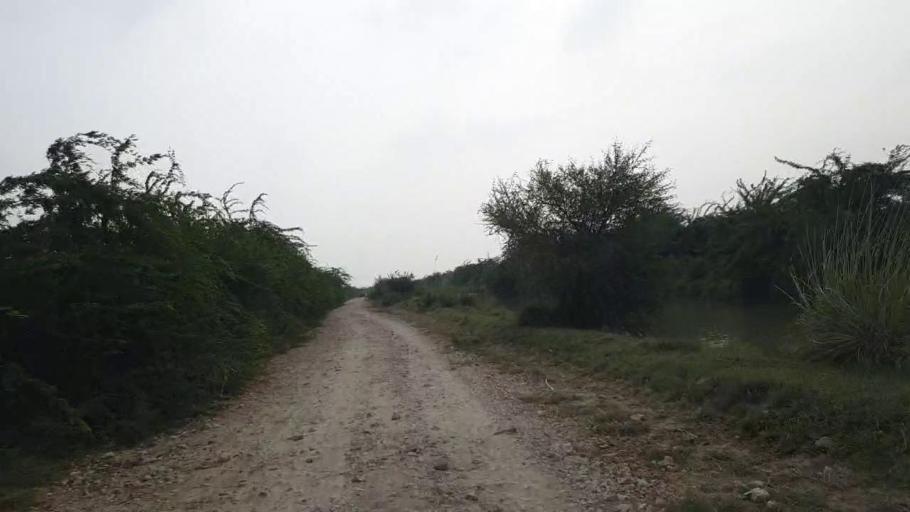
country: PK
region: Sindh
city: Kario
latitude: 24.8591
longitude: 68.5231
